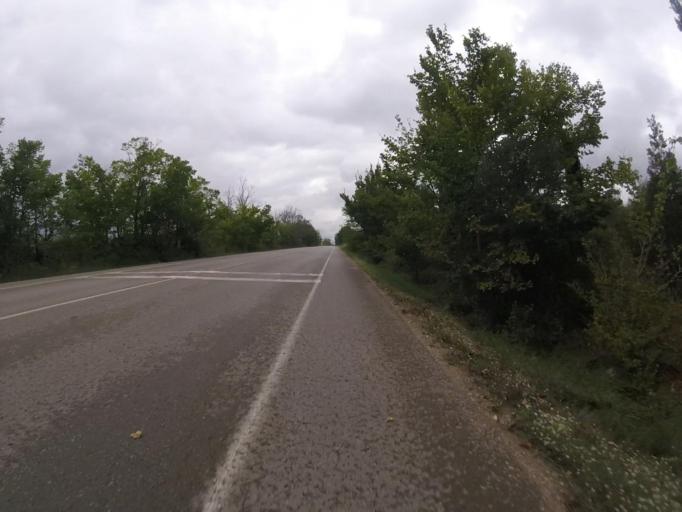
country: ES
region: Valencia
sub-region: Provincia de Castello
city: Cabanes
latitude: 40.1607
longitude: 0.0416
